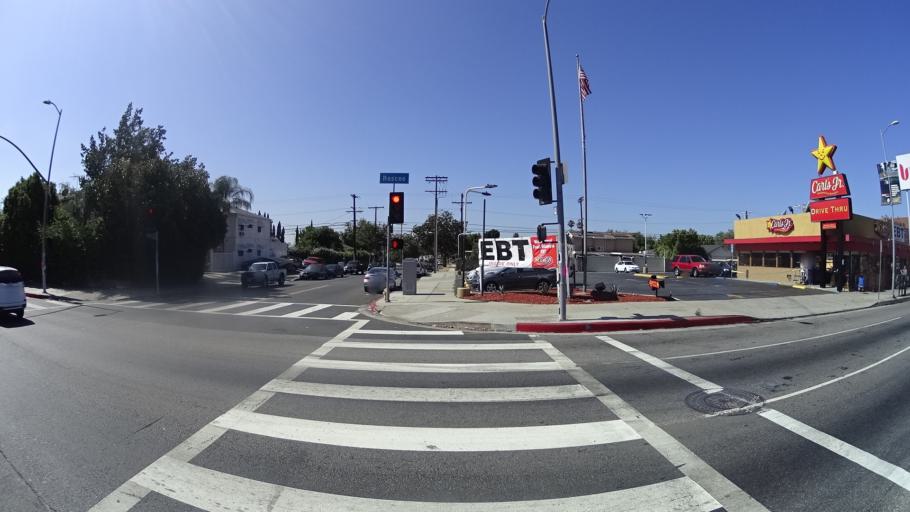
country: US
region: California
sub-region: Los Angeles County
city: Van Nuys
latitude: 34.2216
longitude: -118.4461
